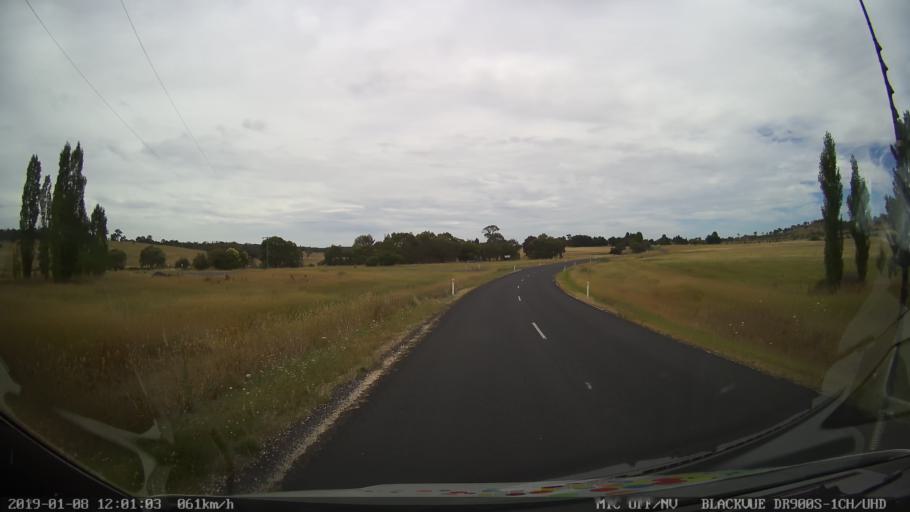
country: AU
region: New South Wales
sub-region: Armidale Dumaresq
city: Armidale
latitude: -30.4615
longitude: 151.6082
